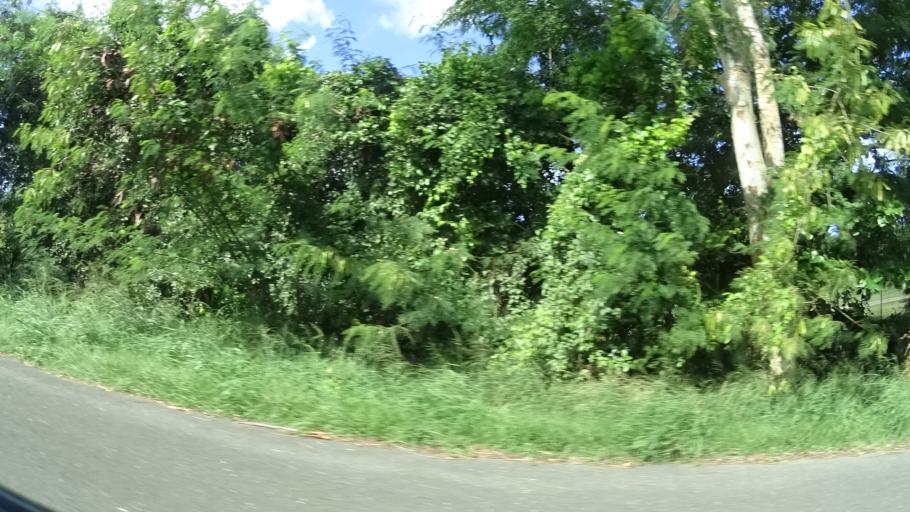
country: PR
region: Luquillo
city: Playa Fortuna
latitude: 18.3760
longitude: -65.7567
